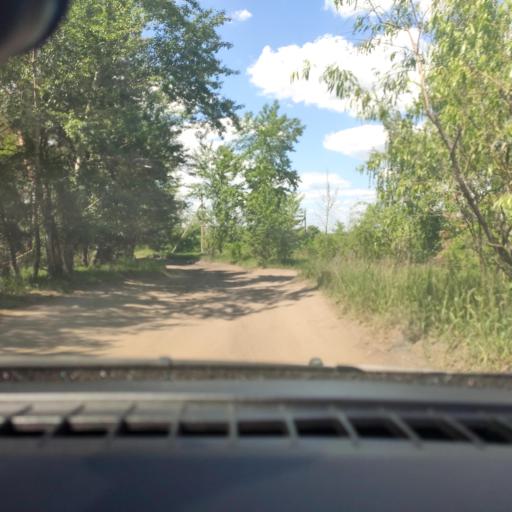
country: RU
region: Voronezj
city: Shilovo
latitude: 51.5349
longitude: 39.1297
